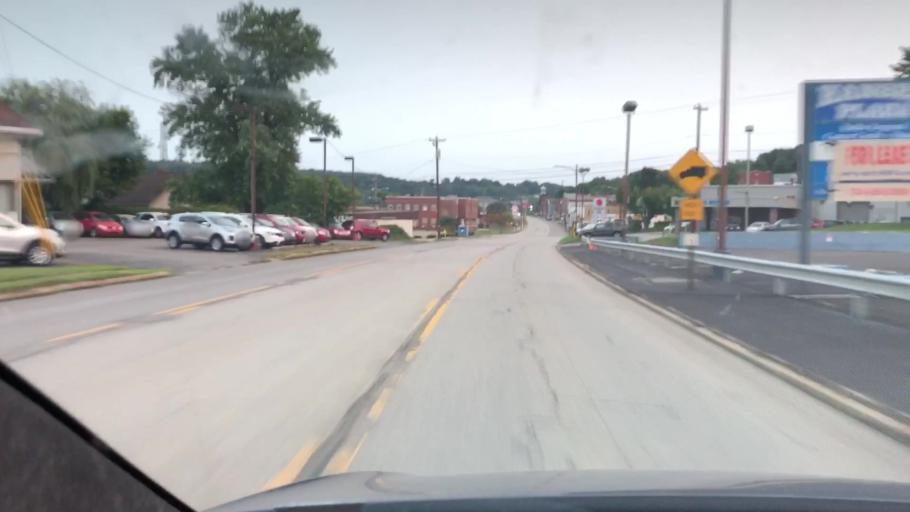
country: US
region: Pennsylvania
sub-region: Butler County
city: Butler
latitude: 40.8597
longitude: -79.9108
